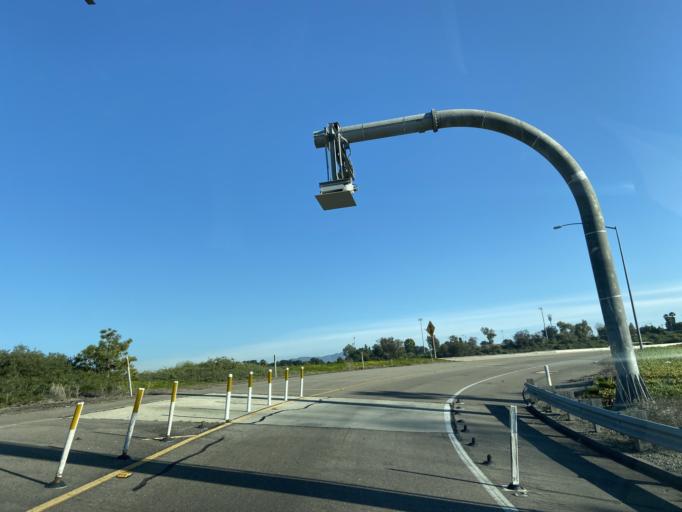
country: US
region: California
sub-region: San Diego County
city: Bonita
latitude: 32.6470
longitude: -116.9717
